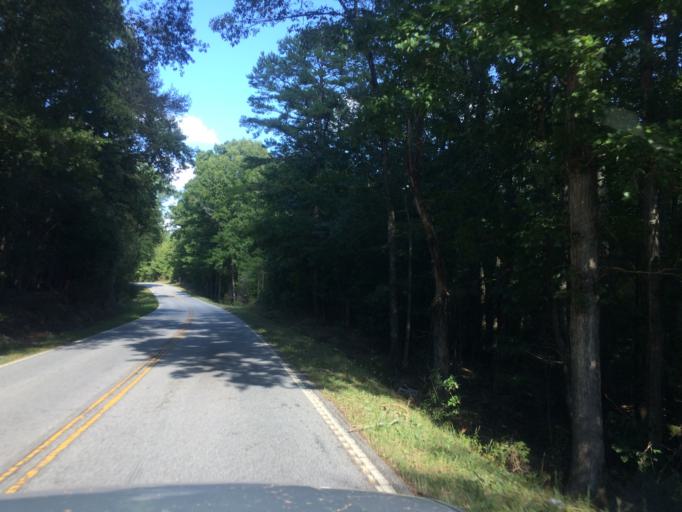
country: US
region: South Carolina
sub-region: Greenwood County
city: Ware Shoals
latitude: 34.4290
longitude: -82.2215
